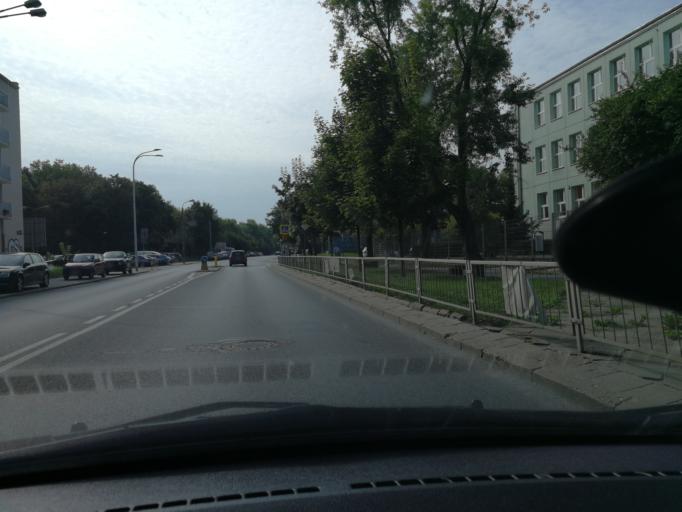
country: PL
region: Masovian Voivodeship
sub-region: Warszawa
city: Bemowo
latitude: 52.2336
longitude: 20.9410
